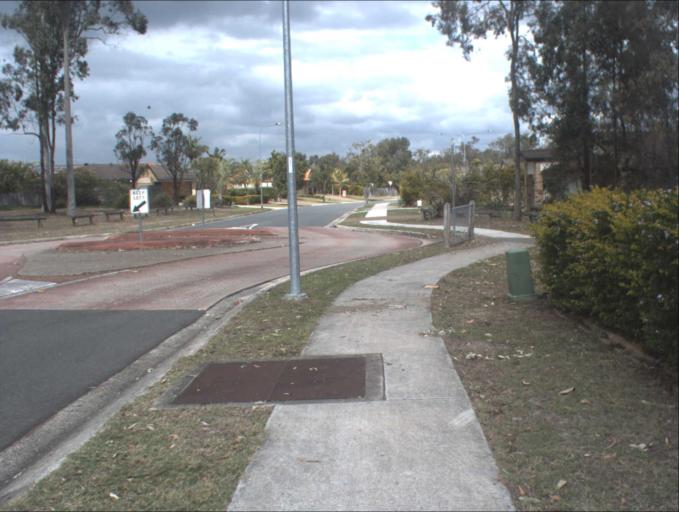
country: AU
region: Queensland
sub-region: Logan
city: Logan Reserve
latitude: -27.6883
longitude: 153.0615
